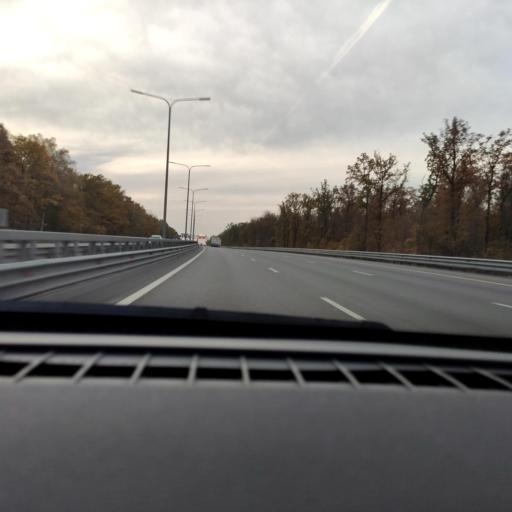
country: RU
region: Voronezj
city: Ramon'
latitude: 51.8315
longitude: 39.2400
